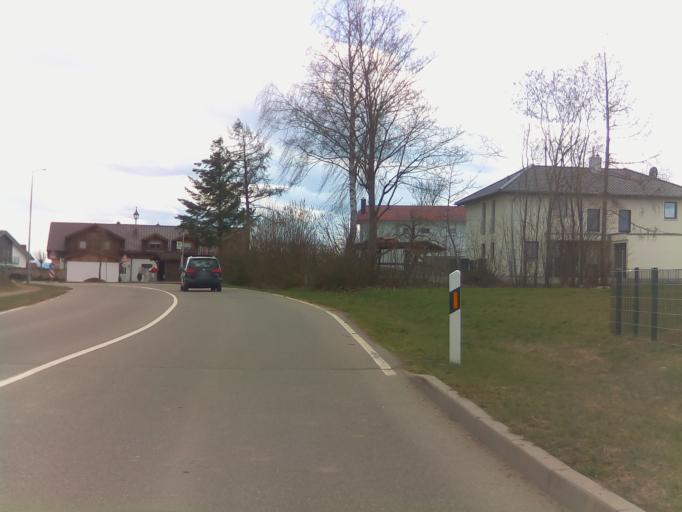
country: DE
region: Baden-Wuerttemberg
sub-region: Regierungsbezirk Stuttgart
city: Alfdorf
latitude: 48.8477
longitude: 9.7129
